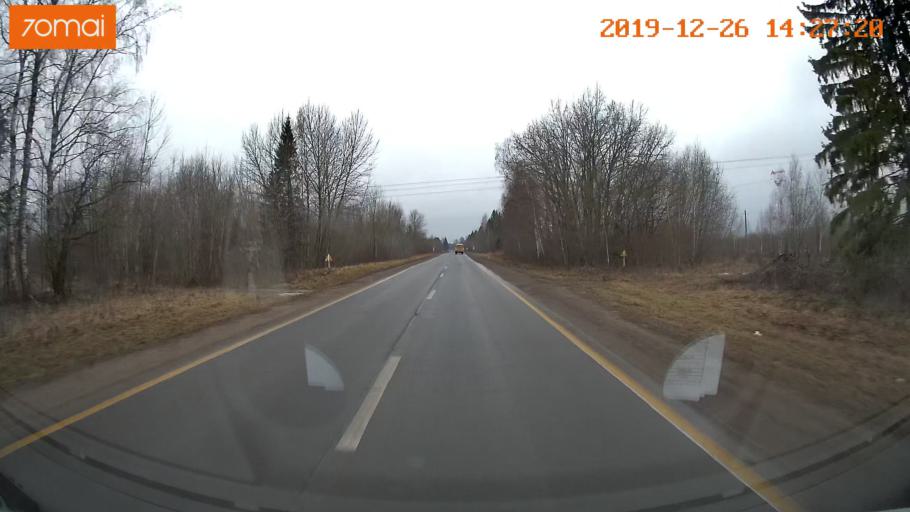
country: RU
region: Jaroslavl
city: Poshekhon'ye
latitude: 58.4834
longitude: 39.0735
